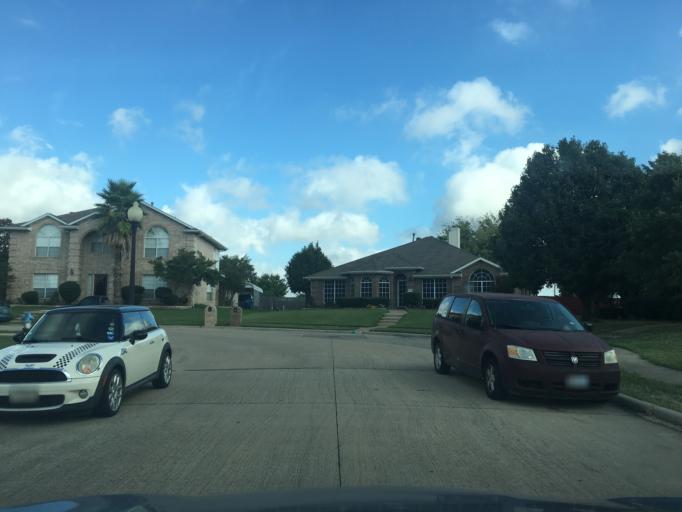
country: US
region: Texas
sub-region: Dallas County
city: Sachse
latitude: 32.9691
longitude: -96.5843
